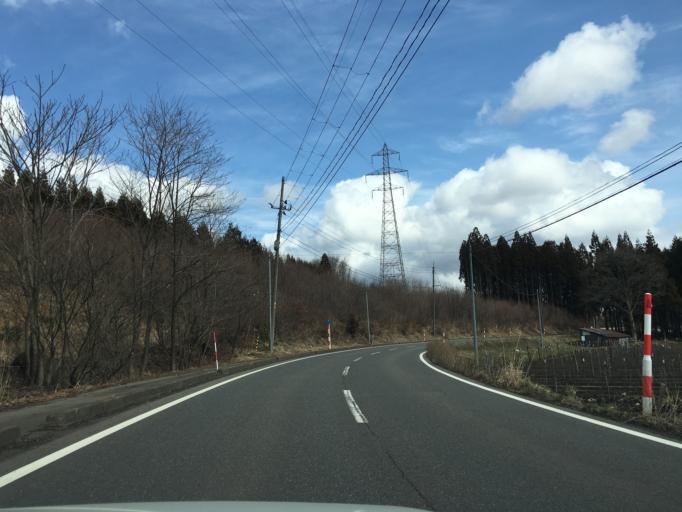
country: JP
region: Akita
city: Odate
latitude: 40.2022
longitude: 140.5418
